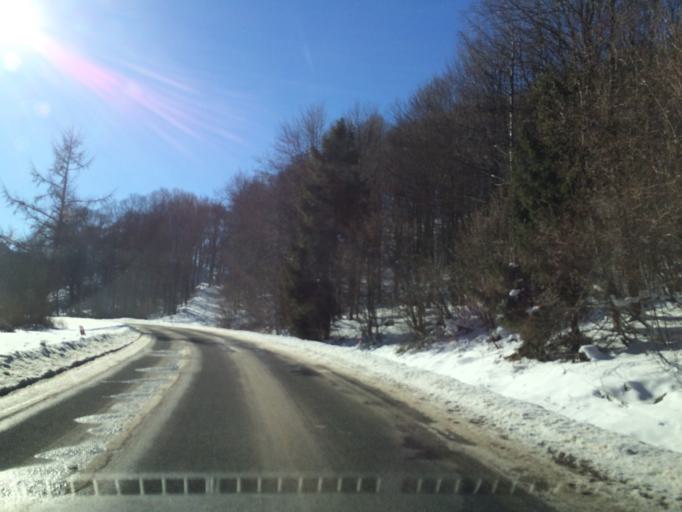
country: PL
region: Subcarpathian Voivodeship
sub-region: Powiat bieszczadzki
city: Lutowiska
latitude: 49.1436
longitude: 22.6680
